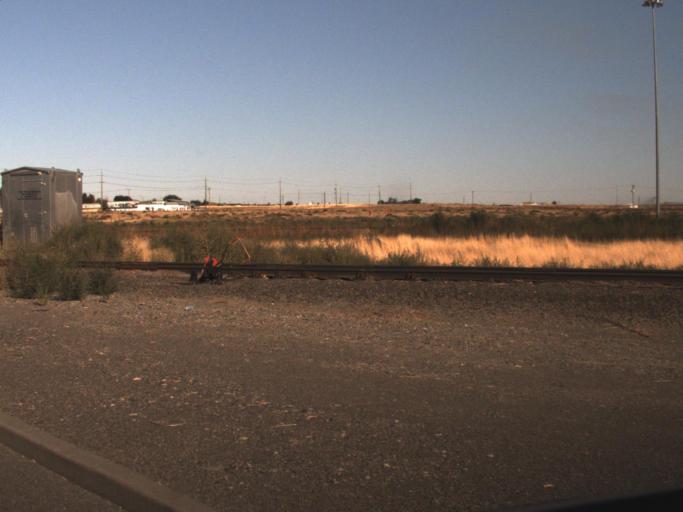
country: US
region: Washington
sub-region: Franklin County
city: Pasco
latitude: 46.2229
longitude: -119.0772
